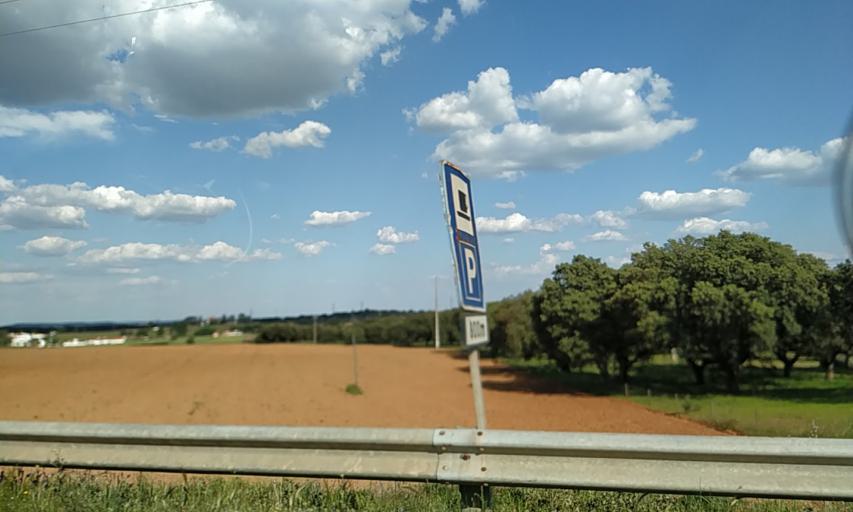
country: PT
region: Evora
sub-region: Estremoz
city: Estremoz
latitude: 38.8889
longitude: -7.5552
